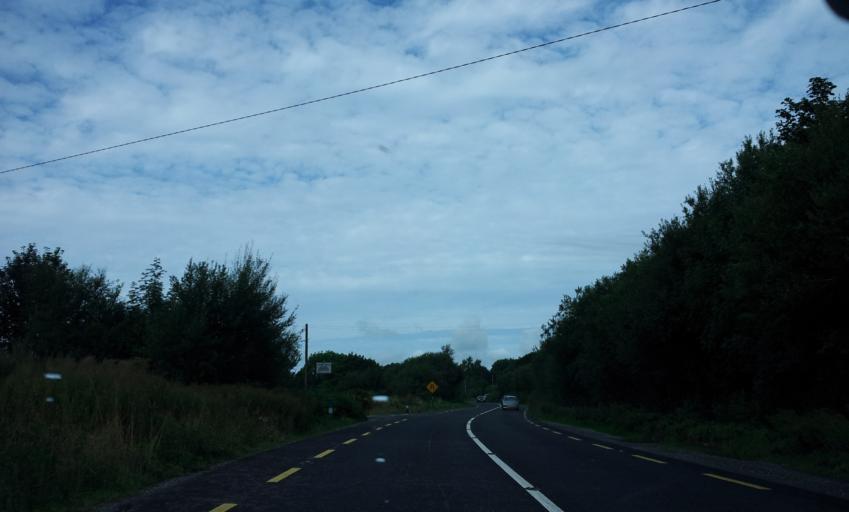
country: IE
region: Munster
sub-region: Ciarrai
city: Cill Airne
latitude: 52.0750
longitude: -9.6466
